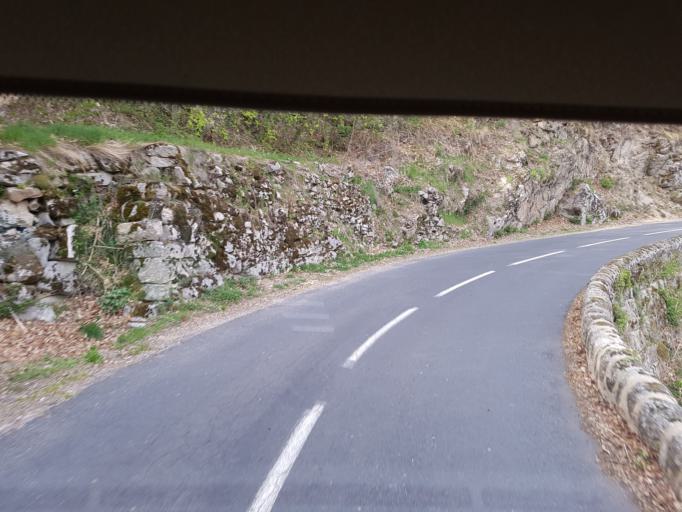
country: FR
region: Languedoc-Roussillon
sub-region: Departement de la Lozere
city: Florac
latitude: 44.3622
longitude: 3.7198
